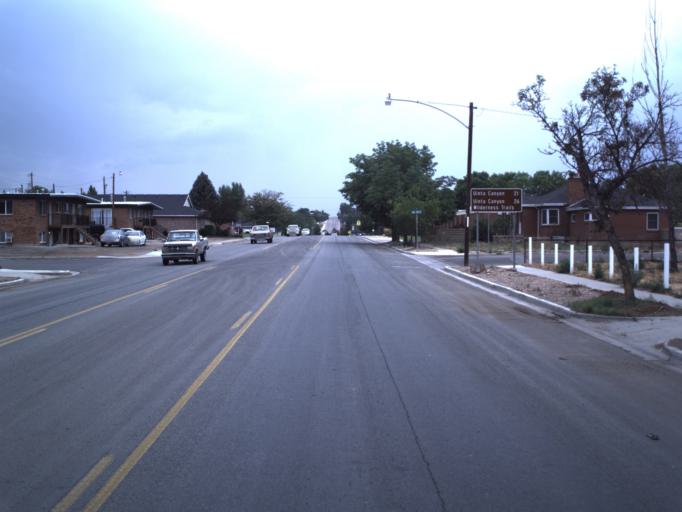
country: US
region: Utah
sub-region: Duchesne County
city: Roosevelt
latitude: 40.3022
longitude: -109.9928
